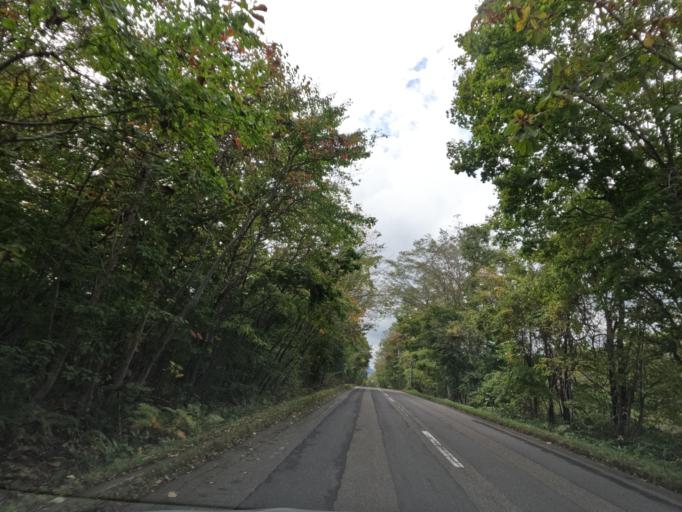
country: JP
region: Hokkaido
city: Chitose
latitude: 42.7922
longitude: 141.5194
